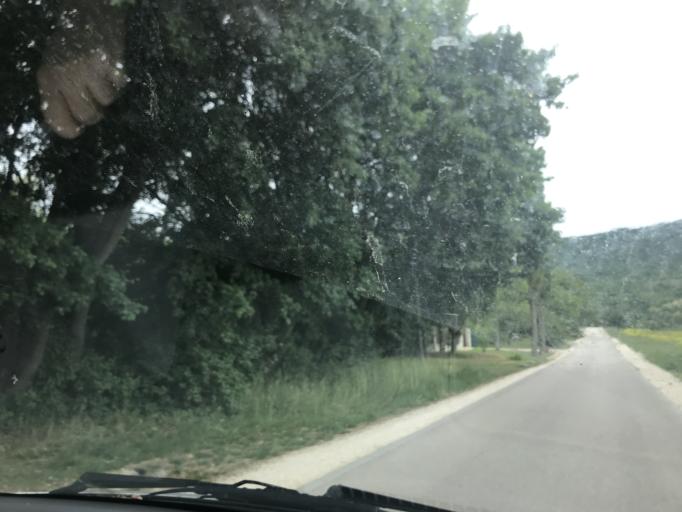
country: HU
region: Pest
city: Pilisszanto
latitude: 47.6513
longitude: 18.9142
